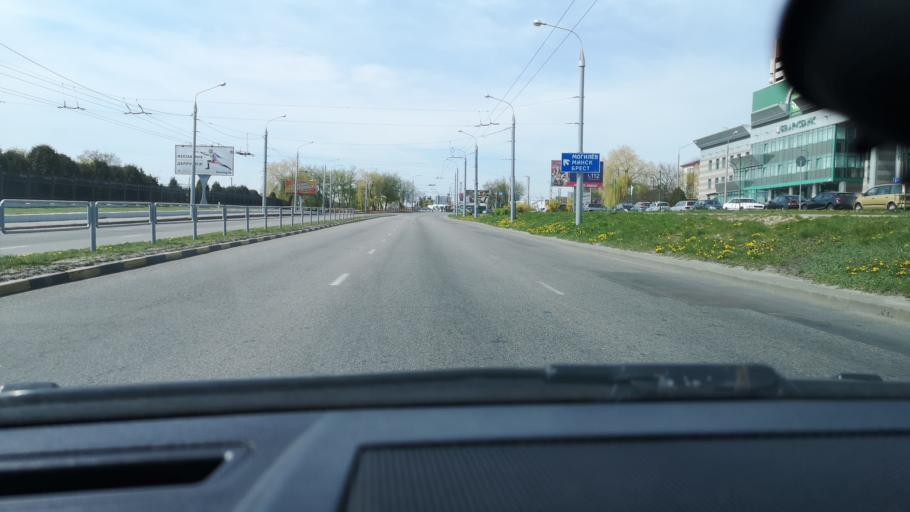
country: BY
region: Gomel
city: Gomel
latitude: 52.4149
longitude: 31.0032
